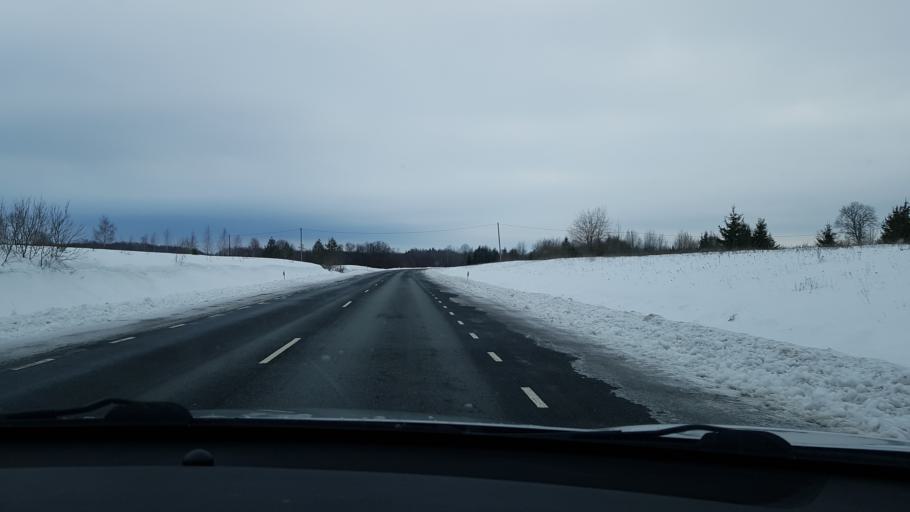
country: EE
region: Jaervamaa
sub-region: Jaerva-Jaani vald
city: Jarva-Jaani
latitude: 58.8995
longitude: 25.7985
